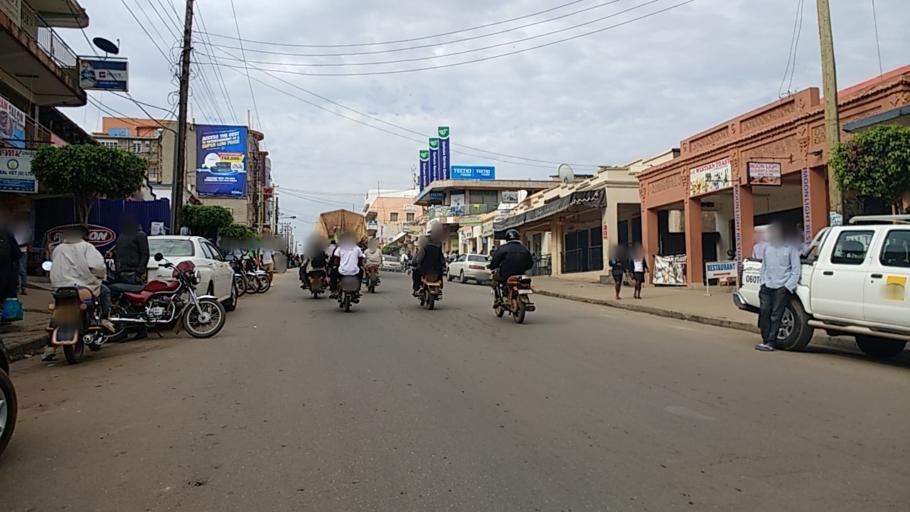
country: UG
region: Western Region
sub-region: Mbarara District
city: Mbarara
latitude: -0.6042
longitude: 30.6628
